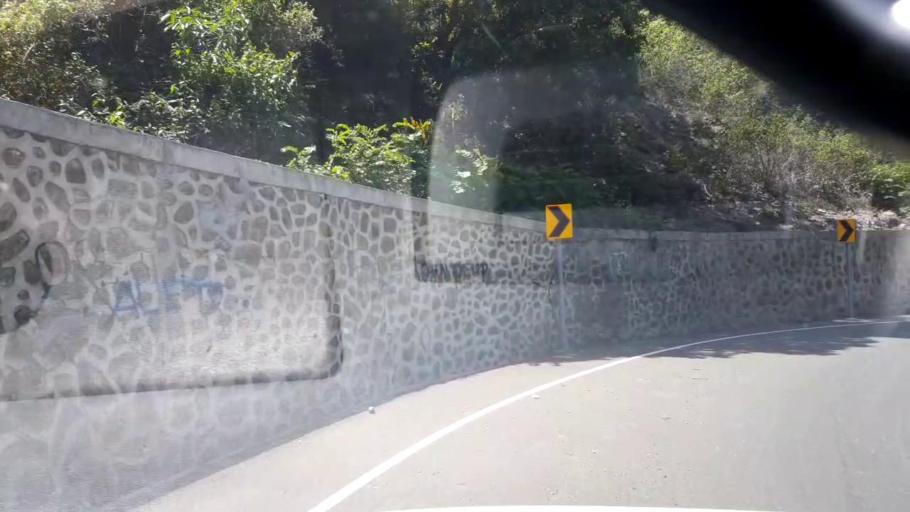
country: TL
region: Liquica
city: Maubara
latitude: -8.6607
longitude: 125.1151
